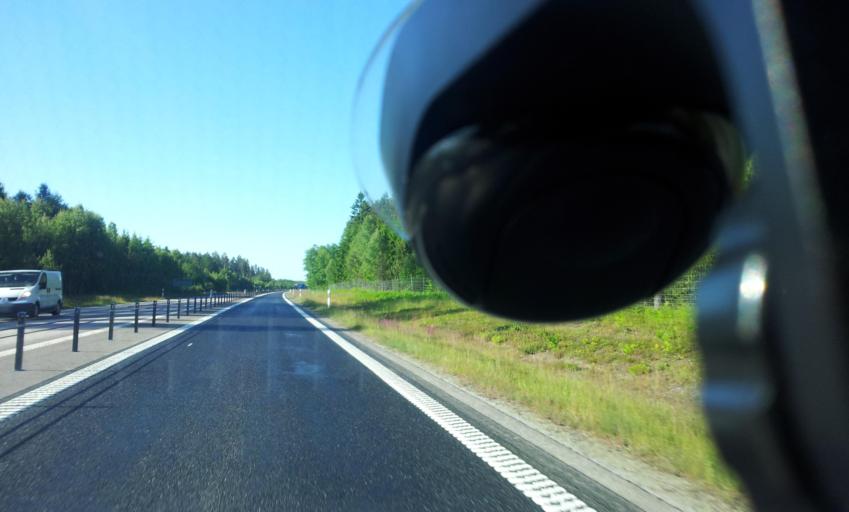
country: SE
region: Kalmar
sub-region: Torsas Kommun
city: Torsas
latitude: 56.5120
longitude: 16.0861
